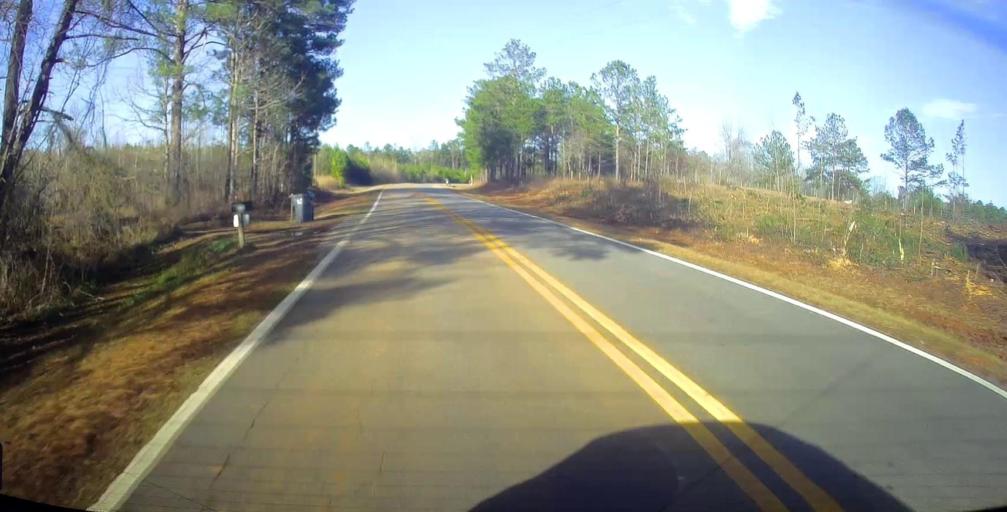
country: US
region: Georgia
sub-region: Crawford County
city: Knoxville
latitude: 32.8289
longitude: -83.9375
